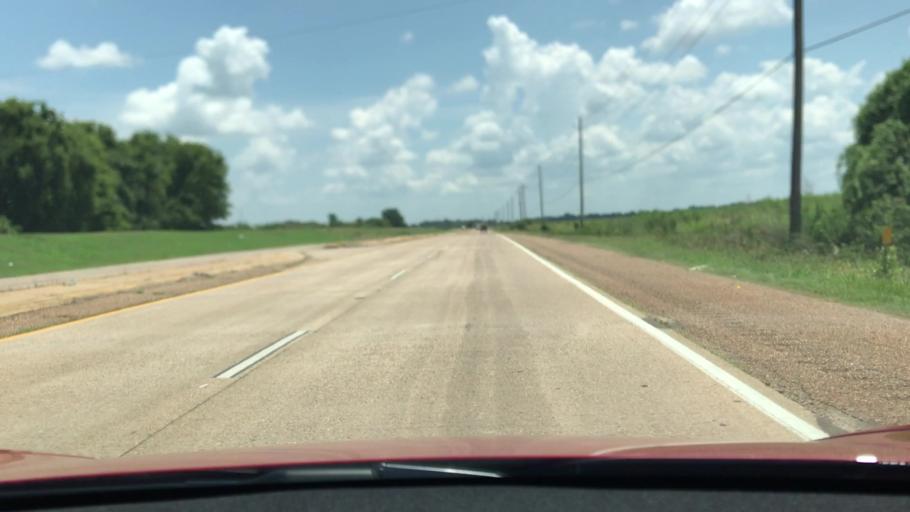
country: US
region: Louisiana
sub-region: Bossier Parish
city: Bossier City
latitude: 32.3956
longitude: -93.6887
